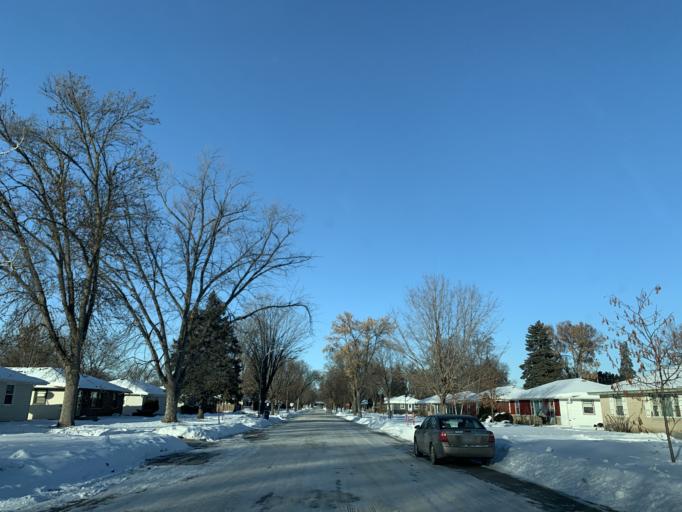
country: US
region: Minnesota
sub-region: Hennepin County
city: Richfield
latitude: 44.8698
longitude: -93.2504
